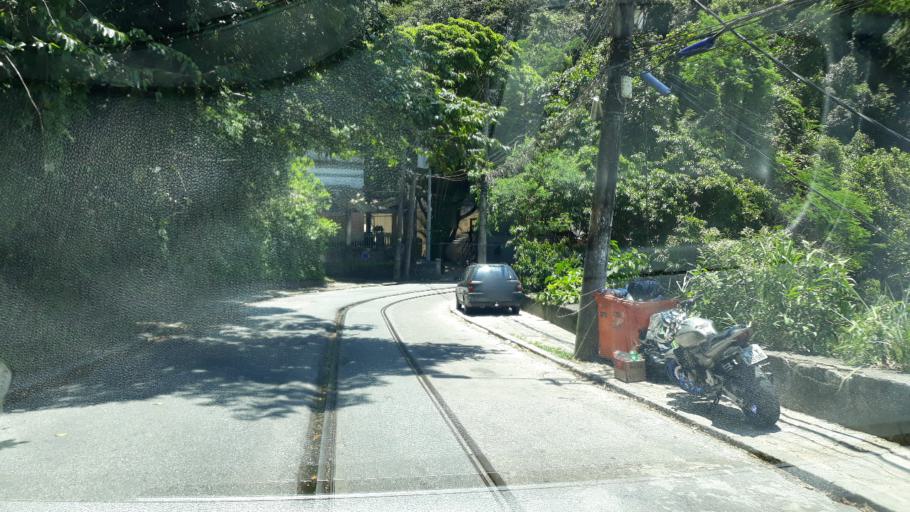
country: BR
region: Rio de Janeiro
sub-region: Rio De Janeiro
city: Rio de Janeiro
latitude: -22.9456
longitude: -43.2080
